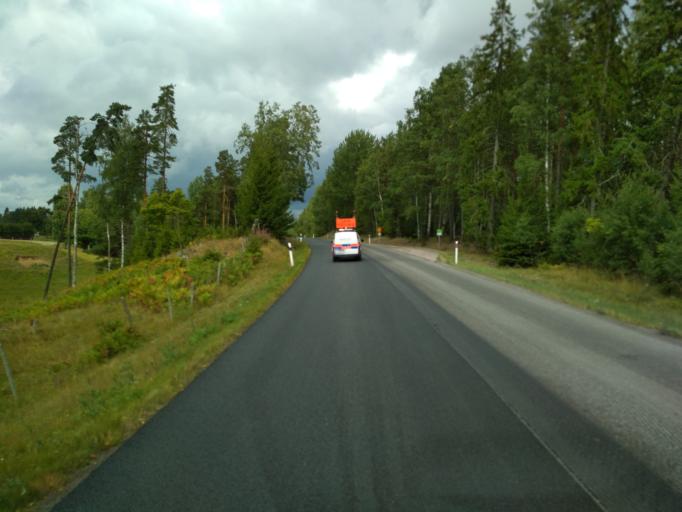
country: SE
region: Soedermanland
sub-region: Flens Kommun
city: Malmkoping
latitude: 59.1605
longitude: 16.6853
